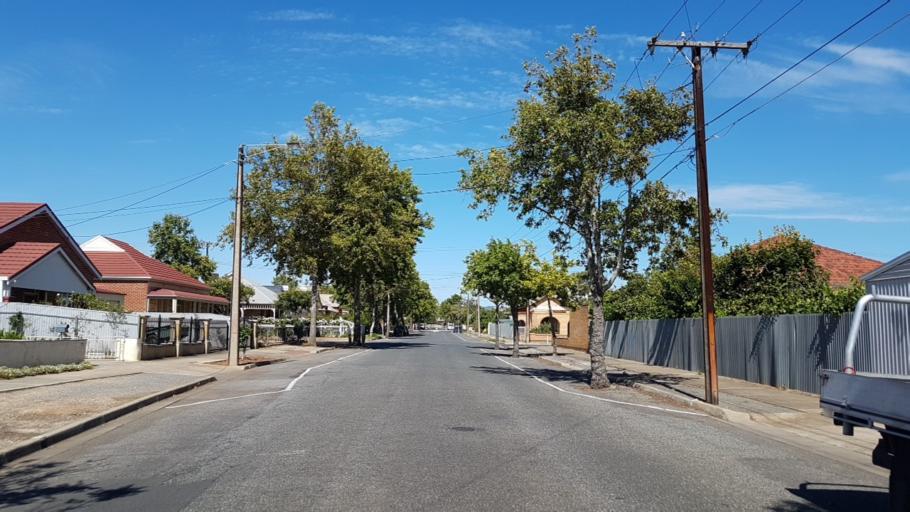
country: AU
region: South Australia
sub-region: City of West Torrens
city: Thebarton
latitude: -34.9202
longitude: 138.5625
